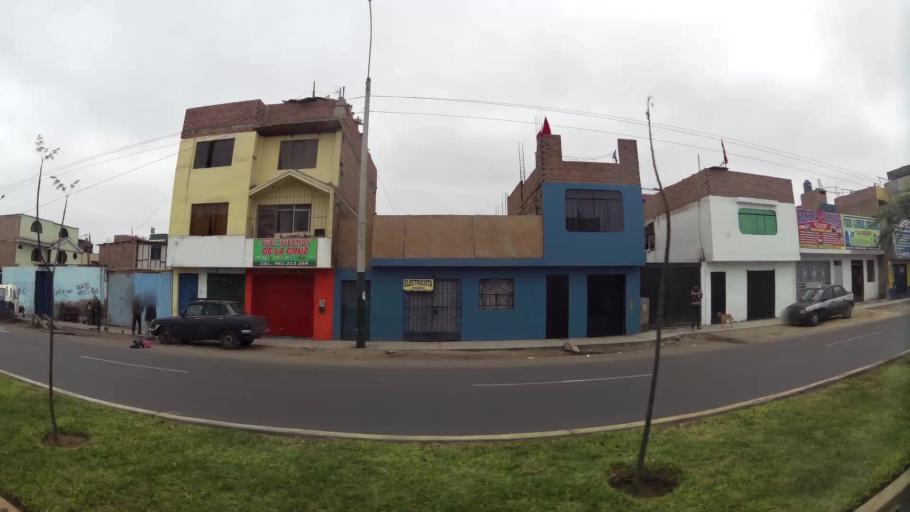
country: PE
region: Lima
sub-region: Lima
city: Surco
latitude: -12.1944
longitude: -76.9808
